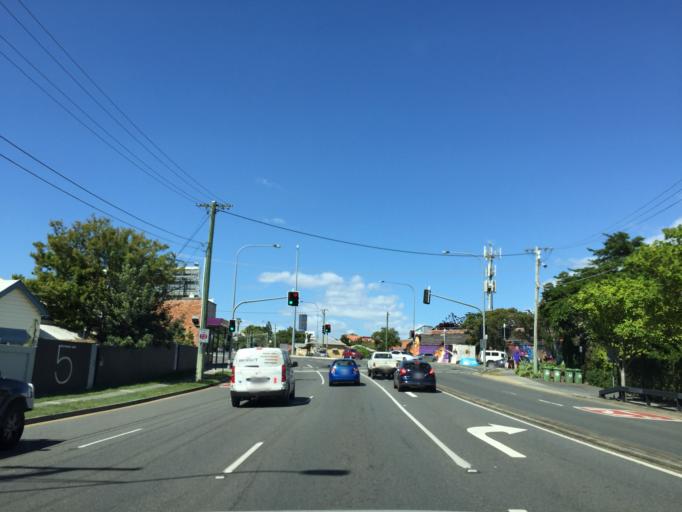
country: AU
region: Queensland
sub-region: Brisbane
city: Milton
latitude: -27.4520
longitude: 153.0040
